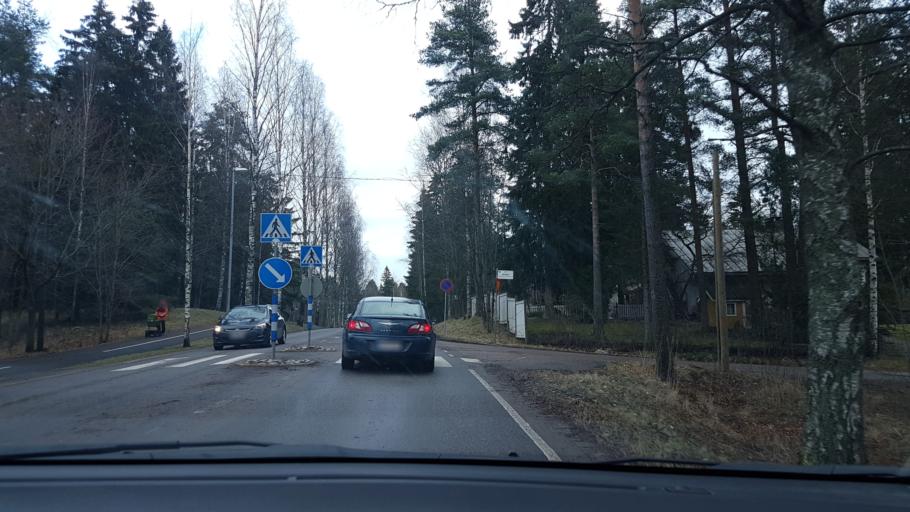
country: FI
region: Uusimaa
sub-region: Helsinki
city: Kerava
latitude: 60.3782
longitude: 25.0838
